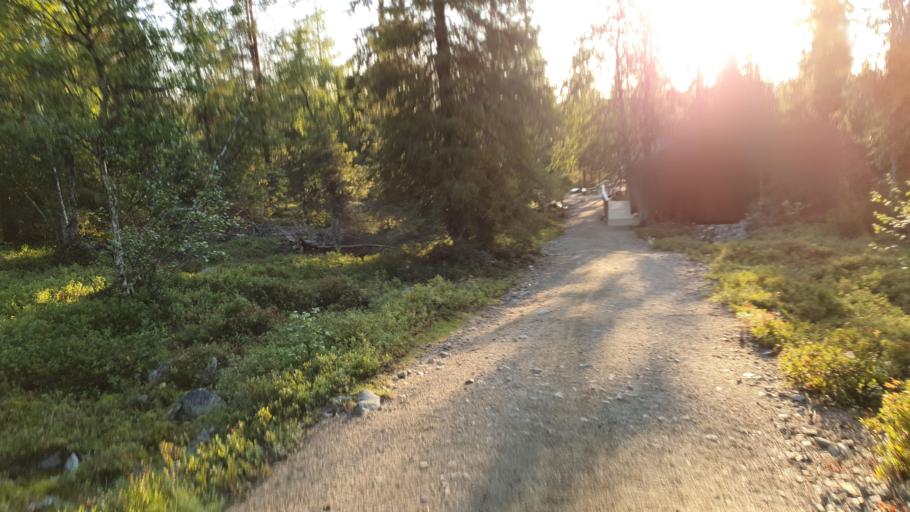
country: FI
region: Lapland
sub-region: Tunturi-Lappi
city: Kolari
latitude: 67.5824
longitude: 24.2289
